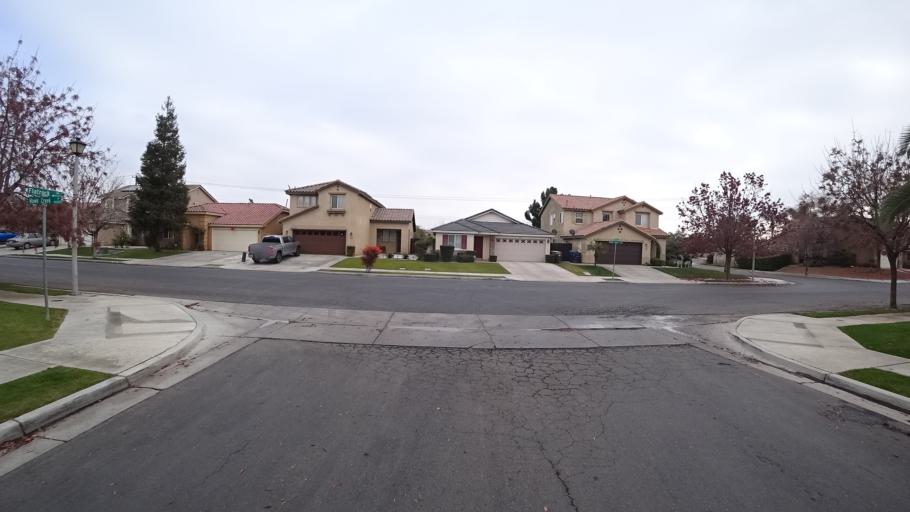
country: US
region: California
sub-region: Kern County
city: Greenfield
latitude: 35.2992
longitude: -119.0753
